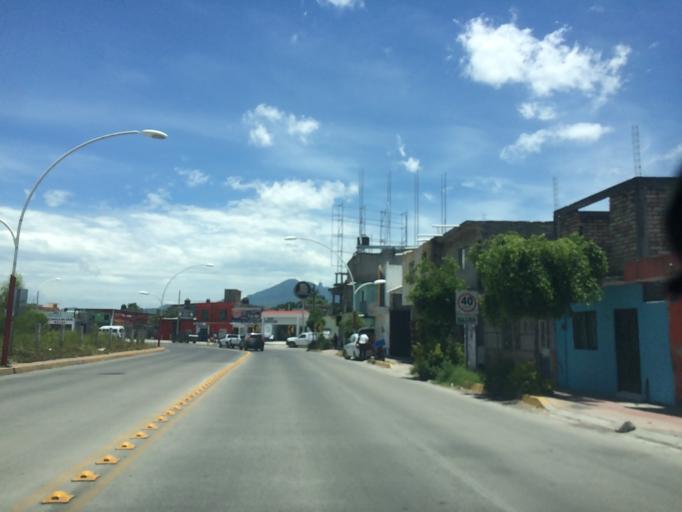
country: MX
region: Nayarit
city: Tepic
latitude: 21.4865
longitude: -104.8671
